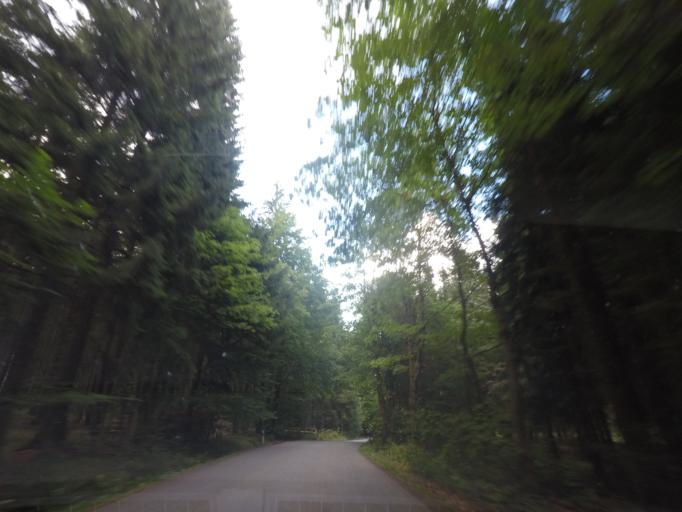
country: CZ
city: Radvanice
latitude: 50.6097
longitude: 16.0596
